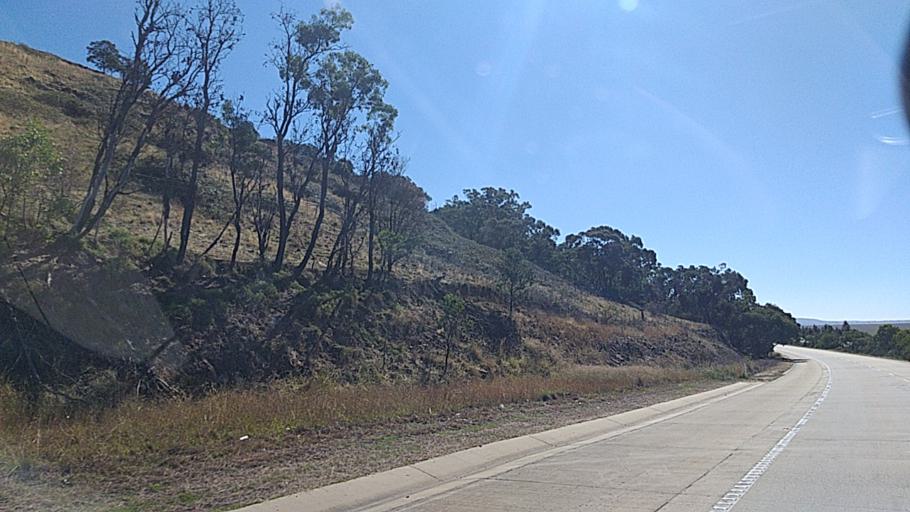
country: AU
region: New South Wales
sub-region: Yass Valley
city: Gundaroo
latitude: -35.0972
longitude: 149.3759
